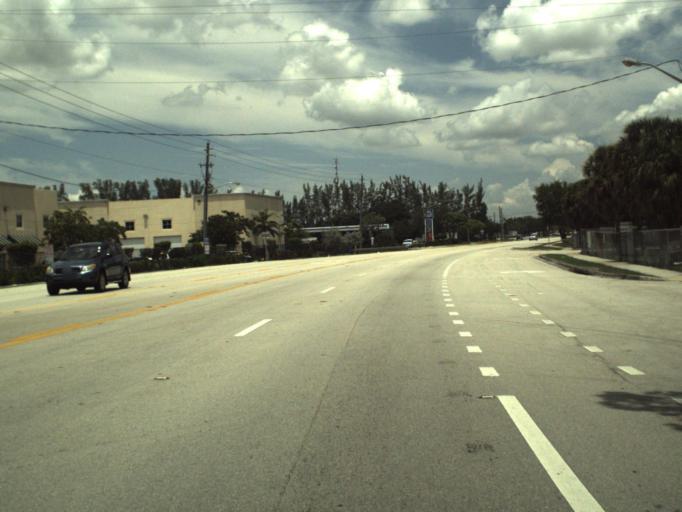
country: US
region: Florida
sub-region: Broward County
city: Coconut Creek
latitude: 26.2402
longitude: -80.1656
